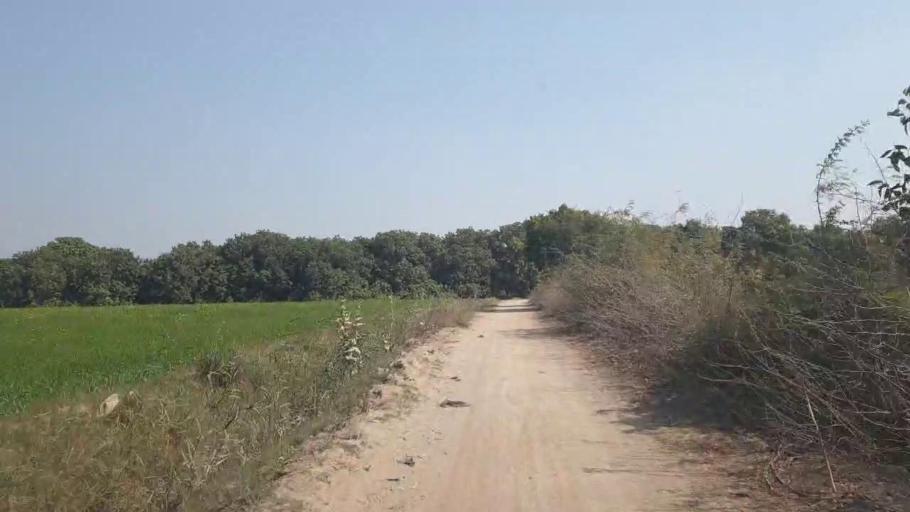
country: PK
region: Sindh
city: Tando Allahyar
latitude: 25.4800
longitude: 68.8490
